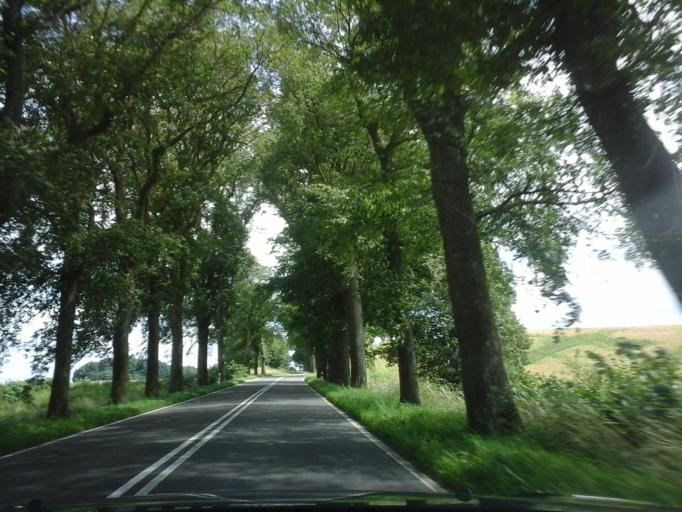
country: PL
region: West Pomeranian Voivodeship
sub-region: Powiat choszczenski
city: Recz
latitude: 53.2826
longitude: 15.5582
